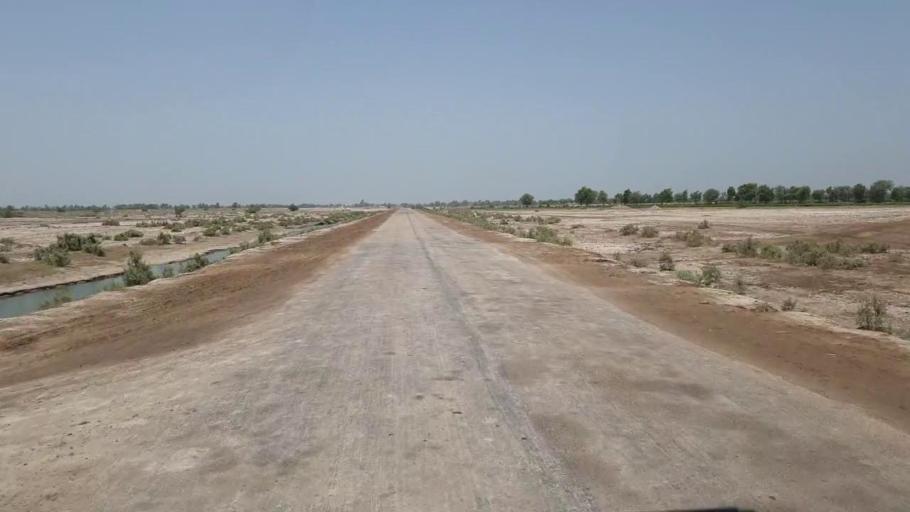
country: PK
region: Sindh
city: Nawabshah
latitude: 26.3652
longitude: 68.4104
